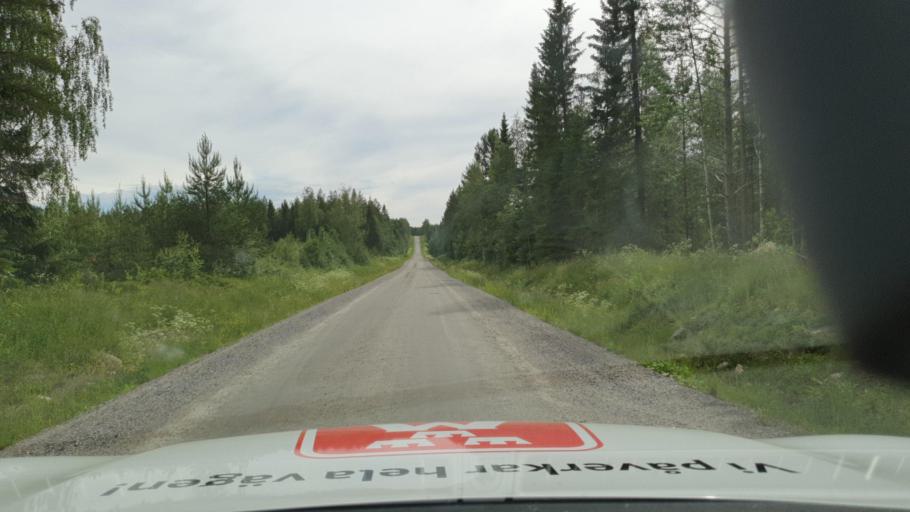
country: SE
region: Vaesterbotten
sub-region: Skelleftea Kommun
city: Burea
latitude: 64.4509
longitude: 21.0257
